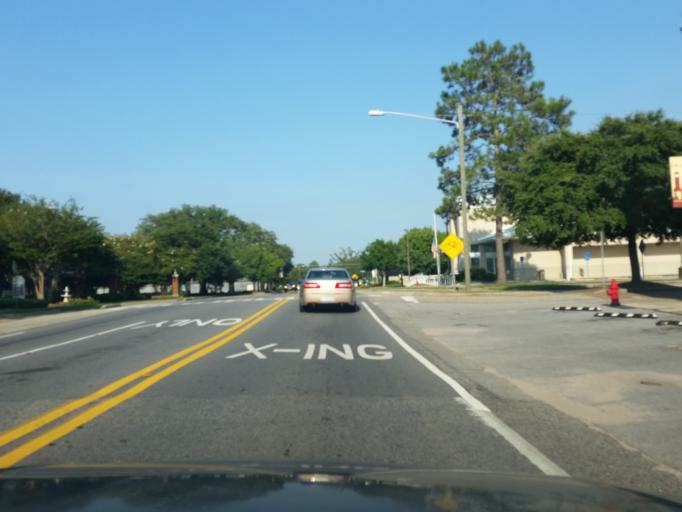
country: US
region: Alabama
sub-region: Baldwin County
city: Foley
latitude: 30.4064
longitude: -87.6835
